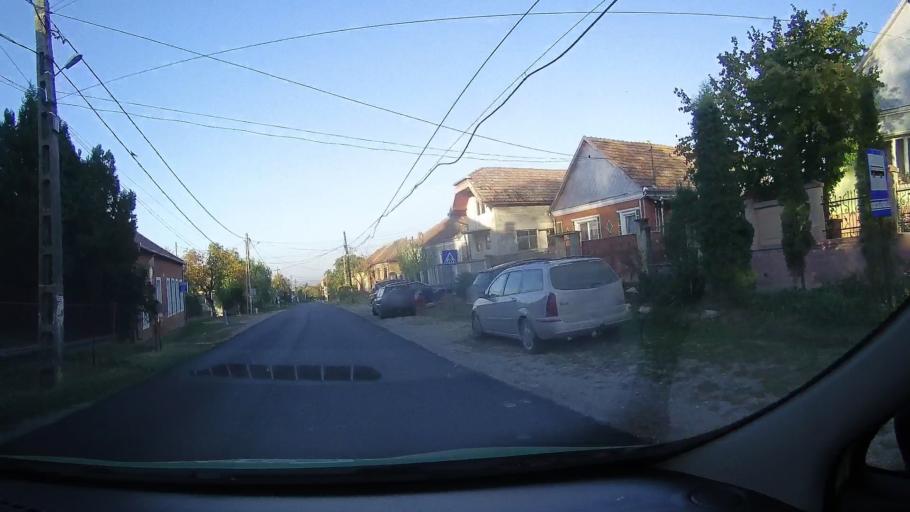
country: RO
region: Bihor
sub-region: Comuna Cetariu
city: Cetariu
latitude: 47.1437
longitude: 21.9989
